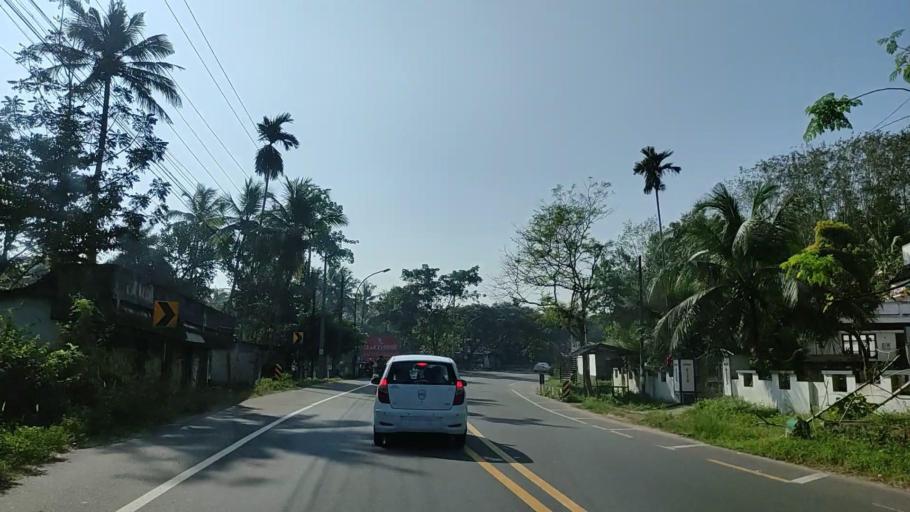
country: IN
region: Kerala
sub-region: Kollam
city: Punalur
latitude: 8.9199
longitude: 76.8553
